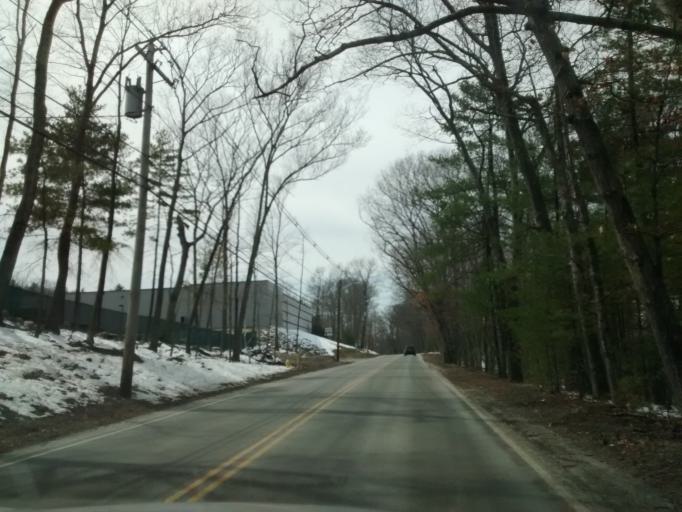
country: US
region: Massachusetts
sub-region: Worcester County
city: Whitinsville
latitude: 42.1083
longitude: -71.6740
